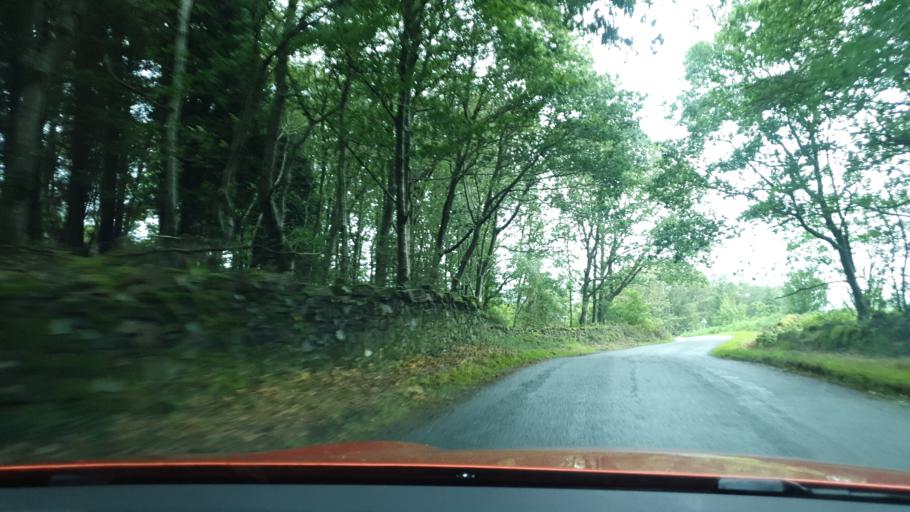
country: GB
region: England
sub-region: Cumbria
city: Seascale
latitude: 54.3995
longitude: -3.3612
